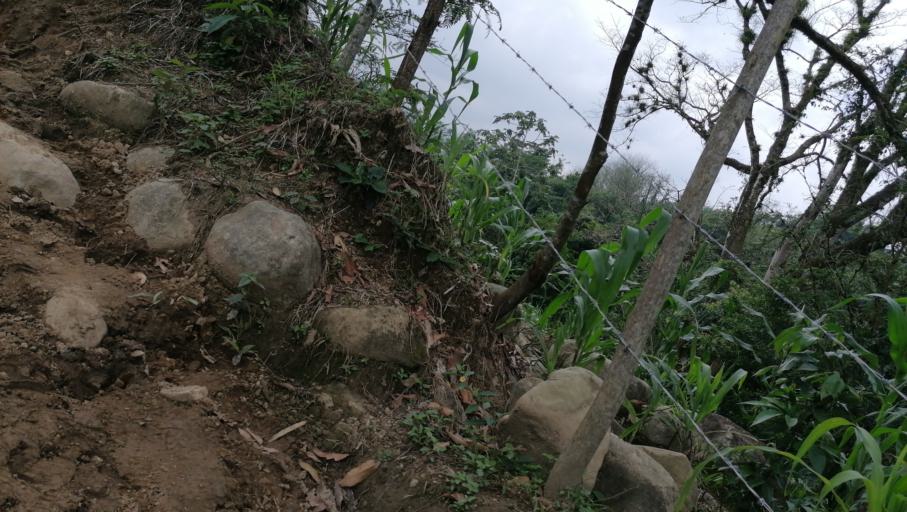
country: MX
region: Chiapas
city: Ocotepec
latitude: 17.2961
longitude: -93.2288
